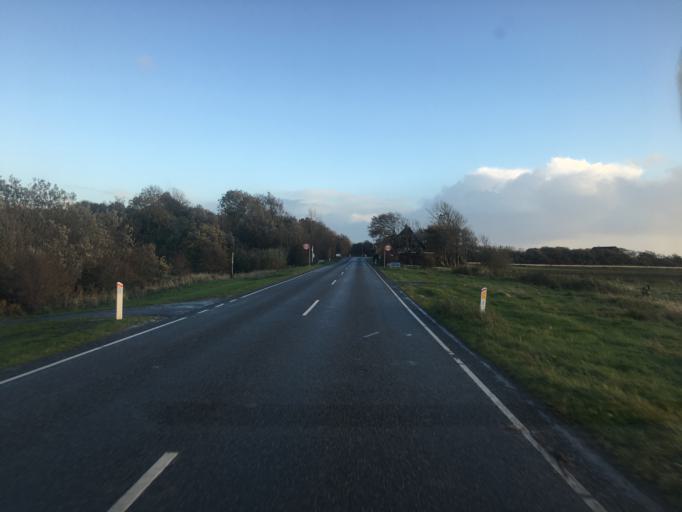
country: DE
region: Schleswig-Holstein
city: Neukirchen
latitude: 54.9088
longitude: 8.7472
